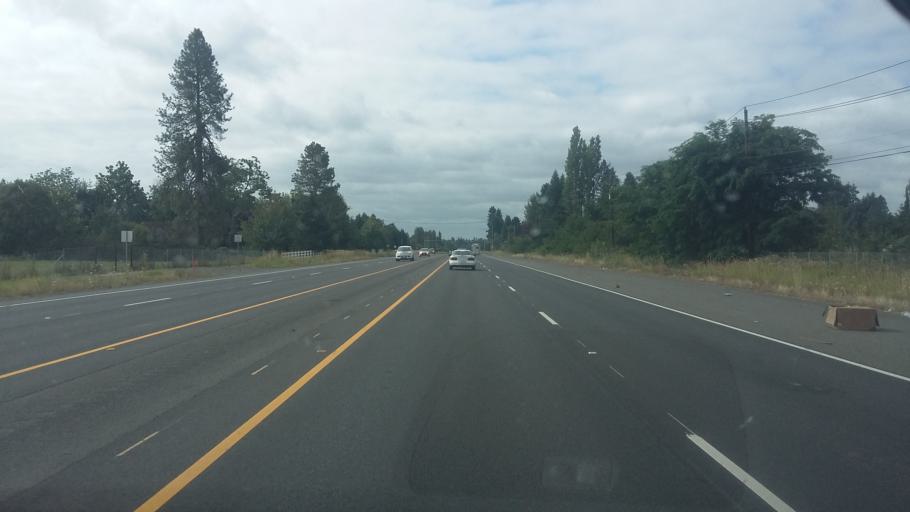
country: US
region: Washington
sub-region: Clark County
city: Meadow Glade
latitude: 45.7627
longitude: -122.5474
